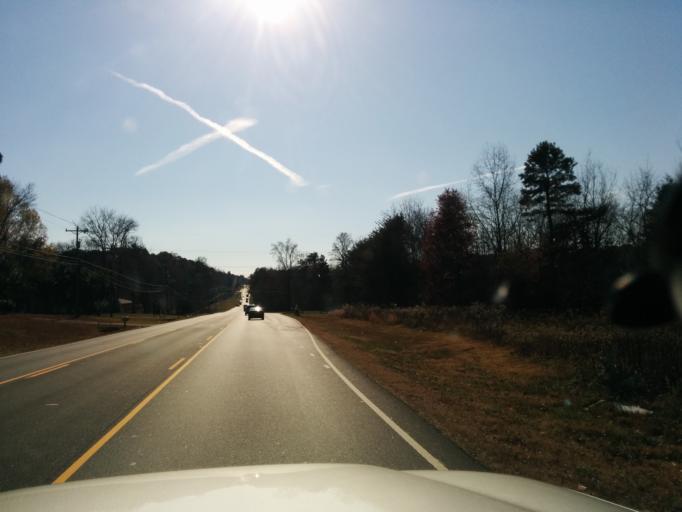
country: US
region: North Carolina
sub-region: Iredell County
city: Mooresville
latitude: 35.5717
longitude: -80.8444
